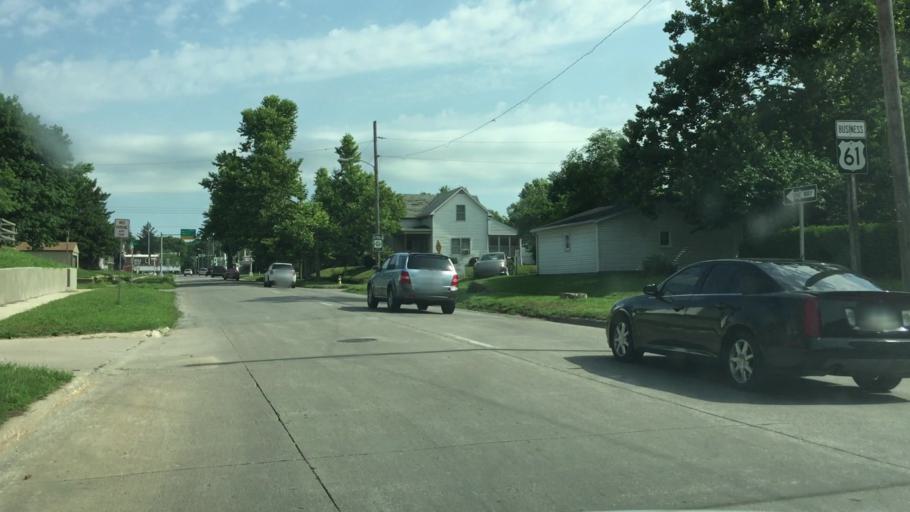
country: US
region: Iowa
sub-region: Lee County
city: Fort Madison
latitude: 40.6276
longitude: -91.3302
